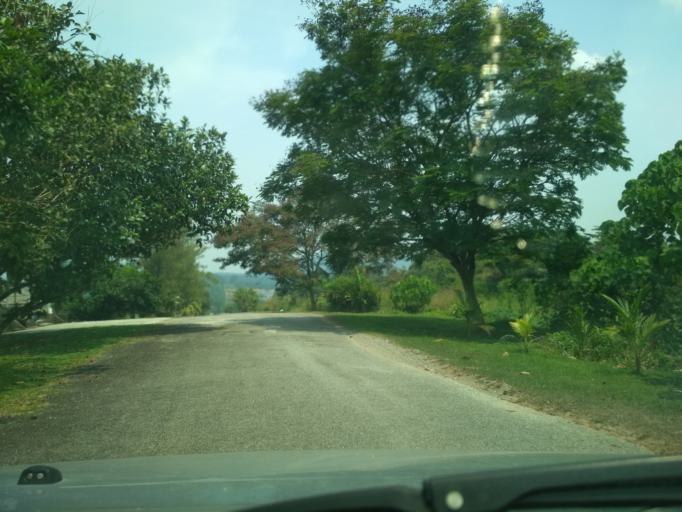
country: MY
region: Kedah
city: Kulim
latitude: 5.3557
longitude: 100.5268
